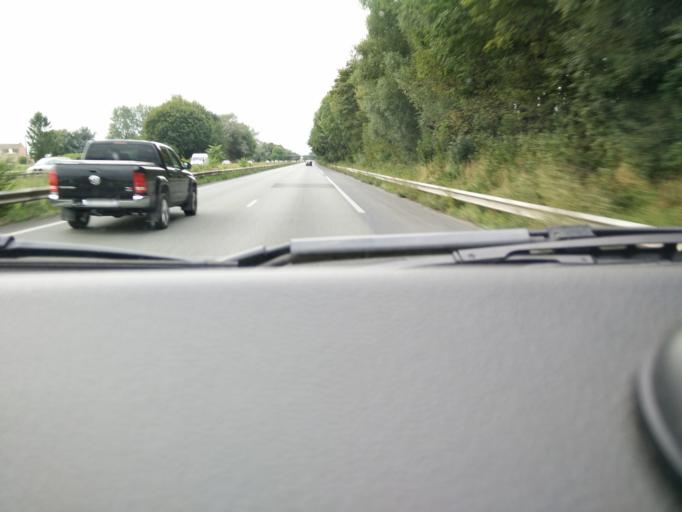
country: FR
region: Nord-Pas-de-Calais
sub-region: Departement du Nord
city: Orchies
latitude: 50.4647
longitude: 3.2470
